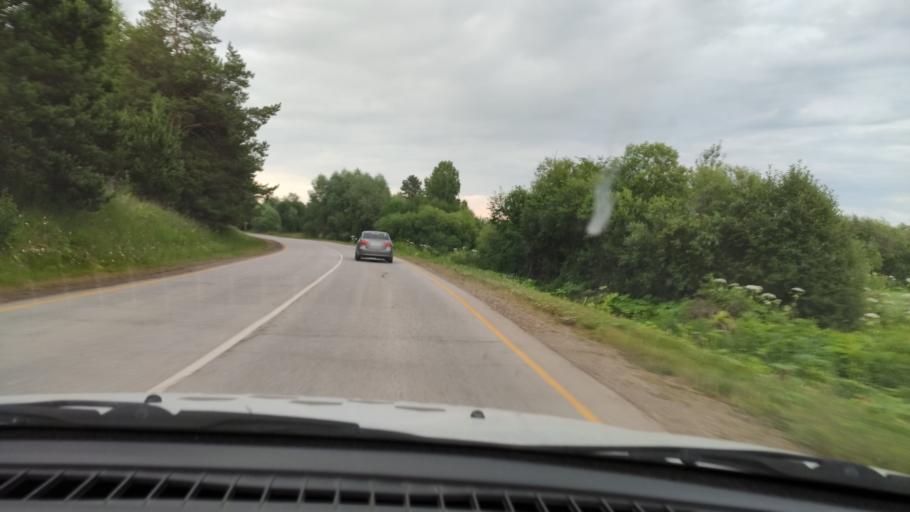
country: RU
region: Perm
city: Kukushtan
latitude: 57.4920
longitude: 56.6382
